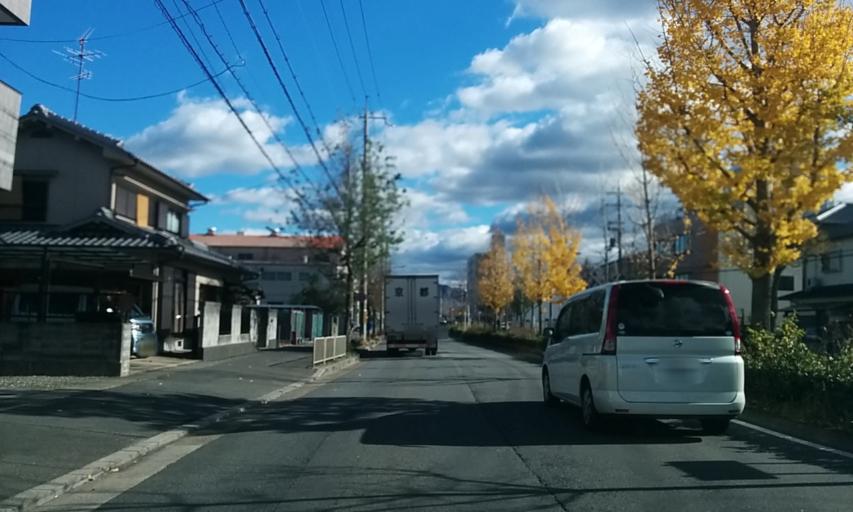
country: JP
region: Kyoto
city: Muko
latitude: 34.9617
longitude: 135.7430
